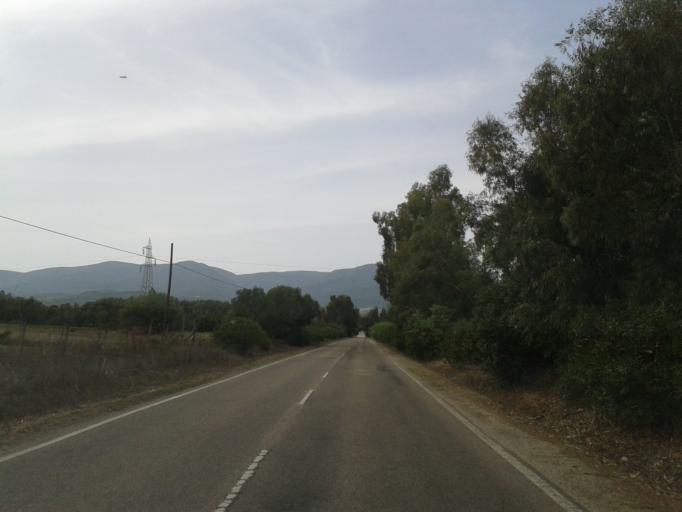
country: IT
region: Sardinia
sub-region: Provincia di Cagliari
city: Olia Speciosa
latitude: 39.2797
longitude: 9.5454
